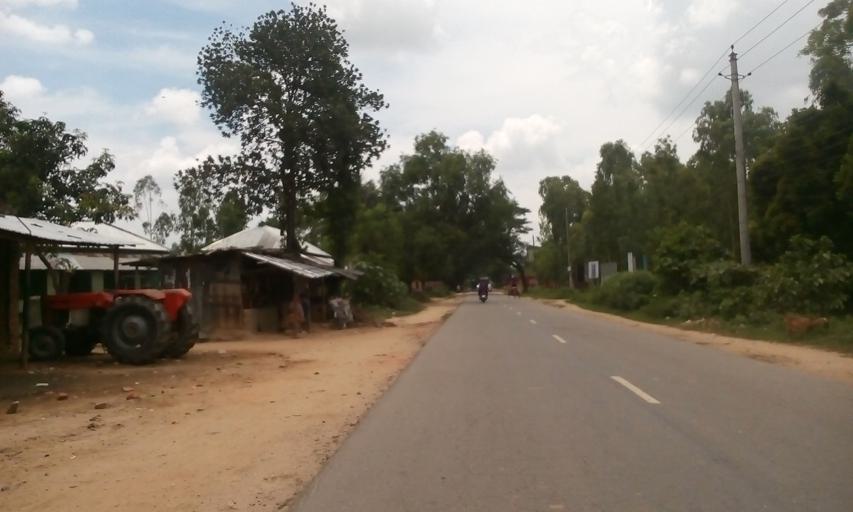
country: BD
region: Rangpur Division
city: Parbatipur
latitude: 25.3975
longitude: 88.9872
